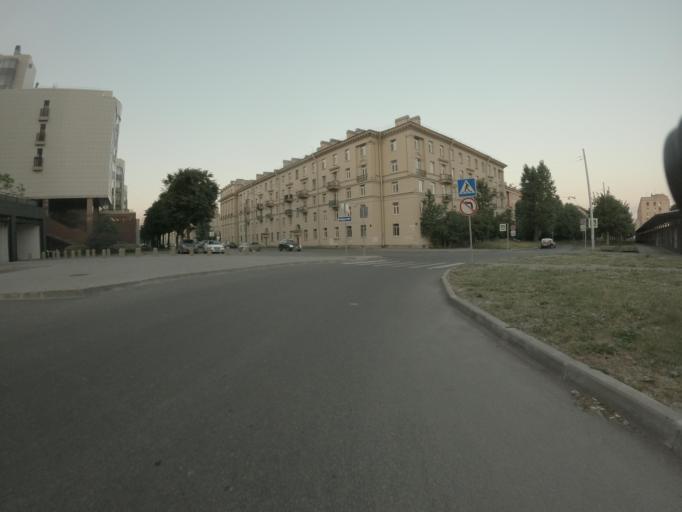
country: RU
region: St.-Petersburg
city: Centralniy
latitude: 59.9306
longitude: 30.4048
